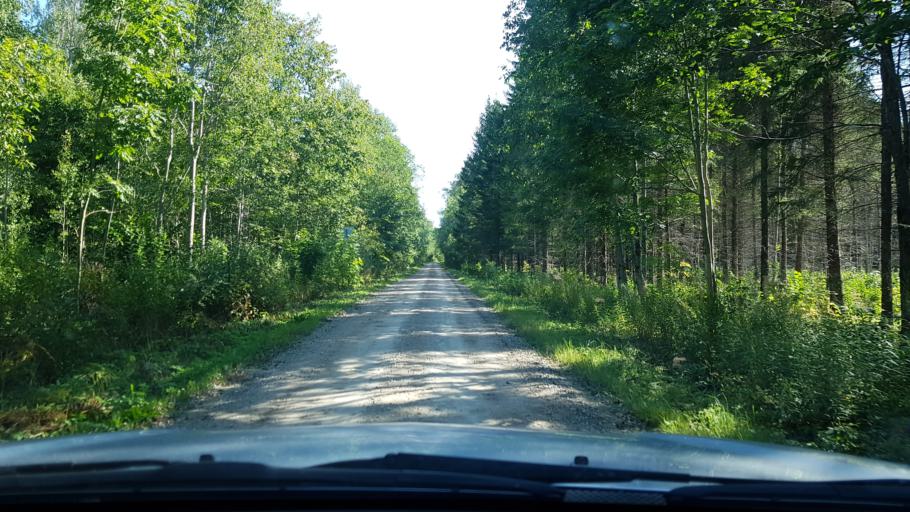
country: EE
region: Ida-Virumaa
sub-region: Sillamaee linn
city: Sillamae
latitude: 59.3323
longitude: 27.7649
